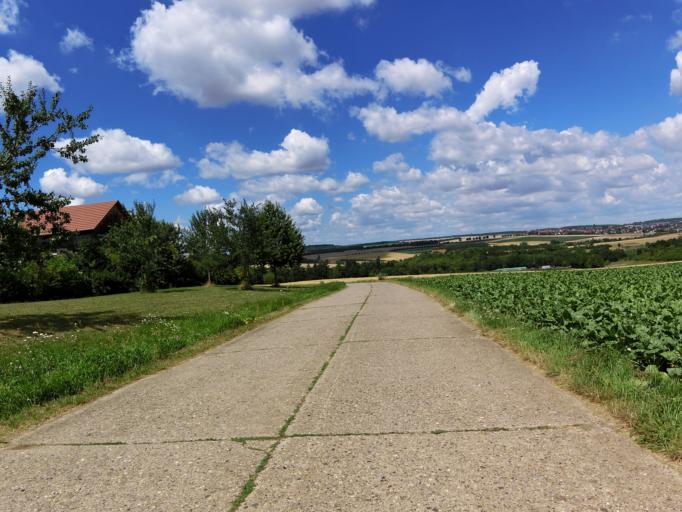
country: DE
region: Bavaria
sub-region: Regierungsbezirk Unterfranken
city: Estenfeld
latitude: 49.8056
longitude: 9.9955
